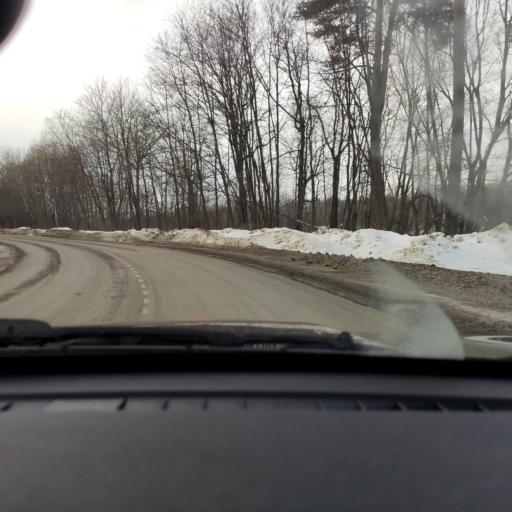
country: RU
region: Samara
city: Pribrezhnyy
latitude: 53.5154
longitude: 49.8510
